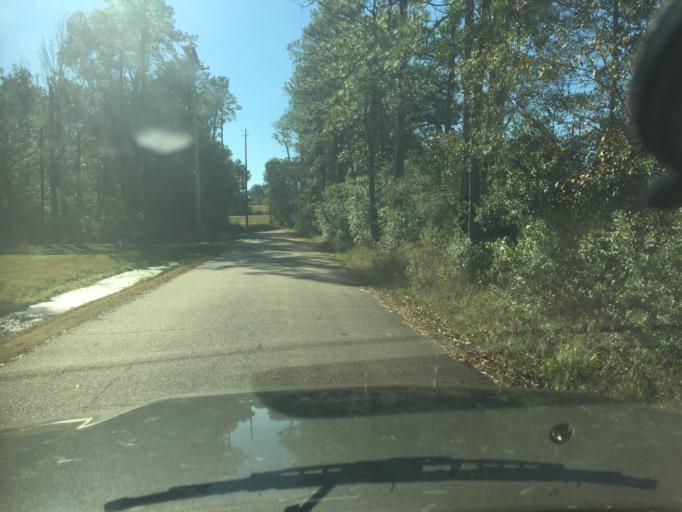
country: US
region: Louisiana
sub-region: Saint Tammany Parish
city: Slidell
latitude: 30.3071
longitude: -89.7377
